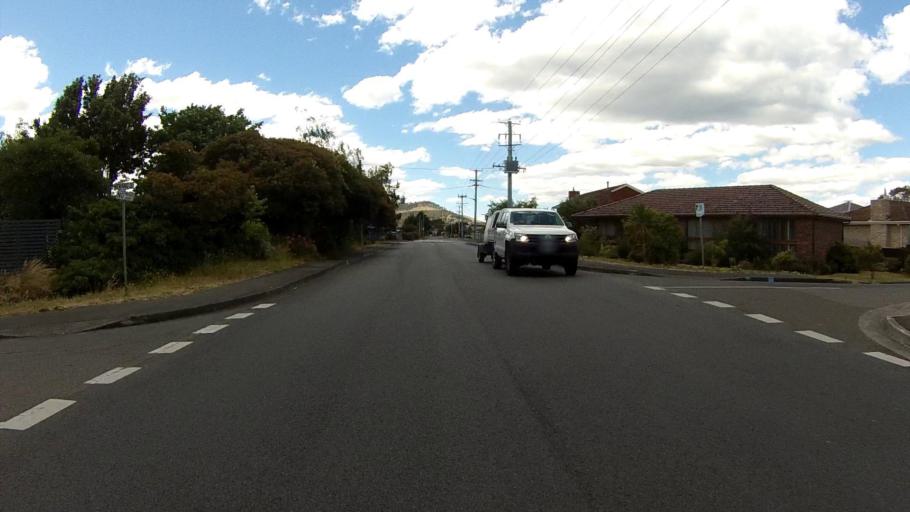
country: AU
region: Tasmania
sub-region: Clarence
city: Lauderdale
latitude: -42.9057
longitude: 147.4929
